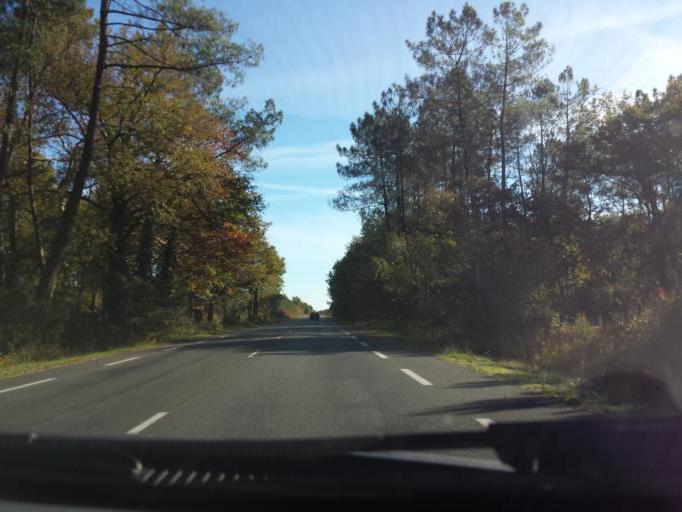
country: FR
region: Aquitaine
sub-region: Departement de la Gironde
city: Sainte-Helene
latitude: 44.9716
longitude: -0.9562
